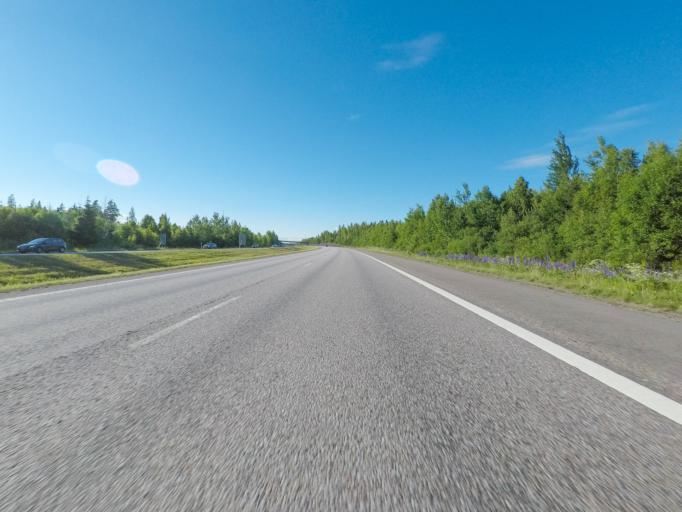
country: FI
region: Uusimaa
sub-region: Helsinki
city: Jaervenpaeae
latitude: 60.4774
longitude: 25.1403
